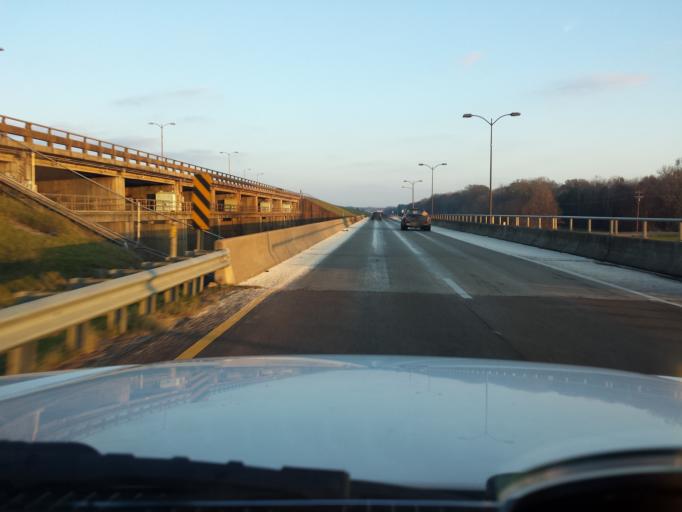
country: US
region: Mississippi
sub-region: Madison County
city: Ridgeland
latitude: 32.3974
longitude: -90.0649
